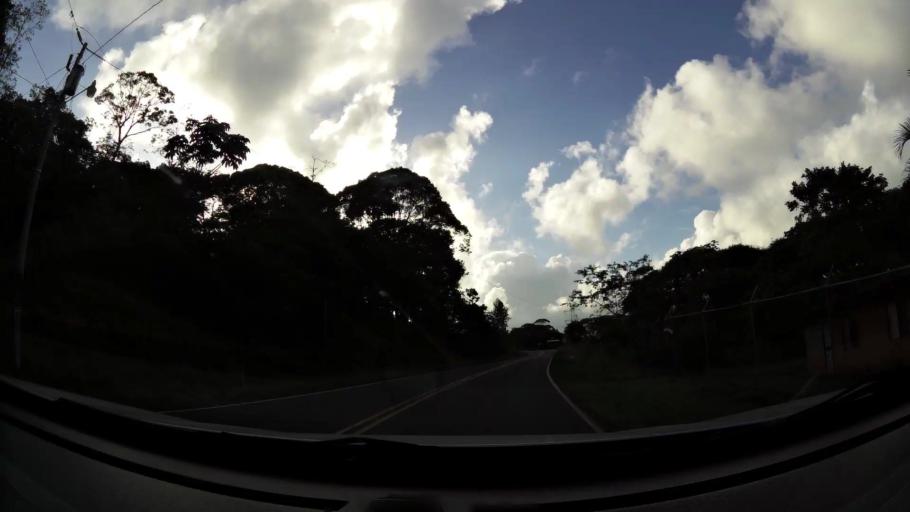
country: CR
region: Limon
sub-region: Canton de Siquirres
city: Siquirres
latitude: 10.0692
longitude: -83.5520
